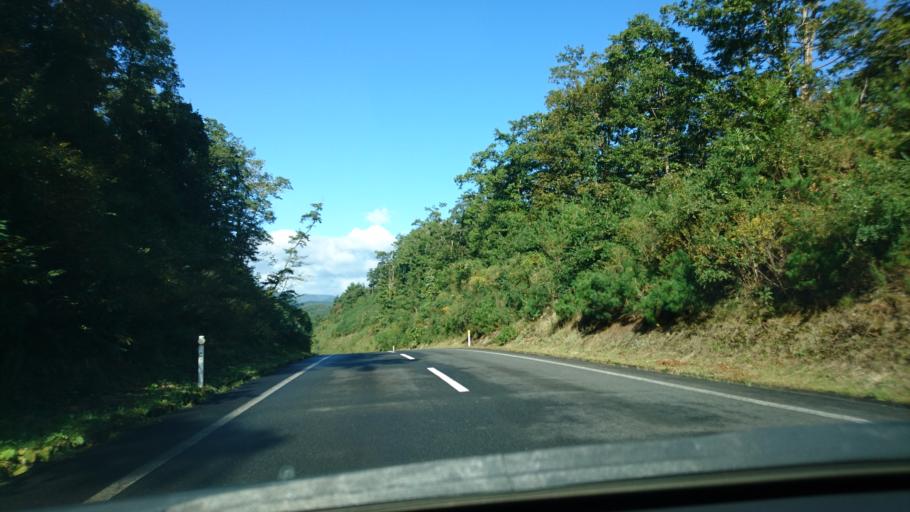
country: JP
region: Iwate
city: Ichinoseki
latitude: 39.0051
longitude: 141.0372
